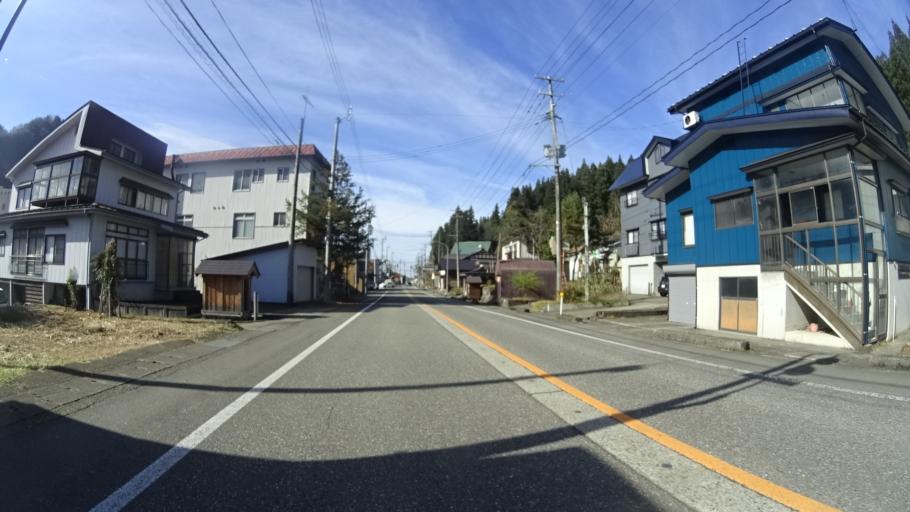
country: JP
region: Niigata
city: Muikamachi
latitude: 37.2076
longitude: 139.0638
